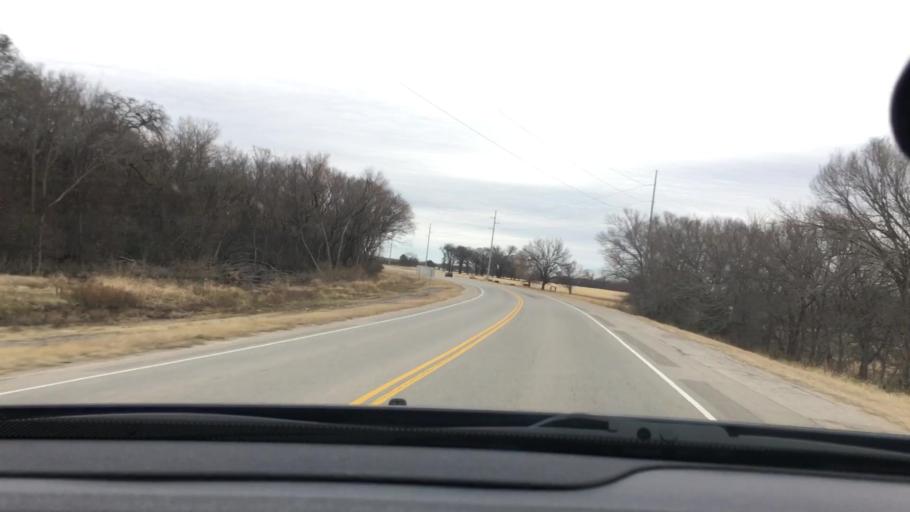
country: US
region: Oklahoma
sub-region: Marshall County
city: Oakland
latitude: 34.1911
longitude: -96.8028
